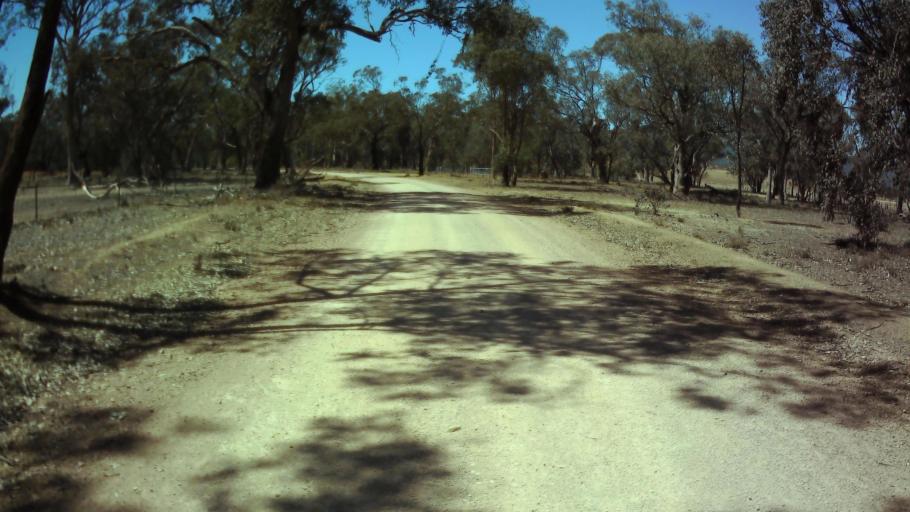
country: AU
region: New South Wales
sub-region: Weddin
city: Grenfell
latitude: -33.9368
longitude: 148.0775
